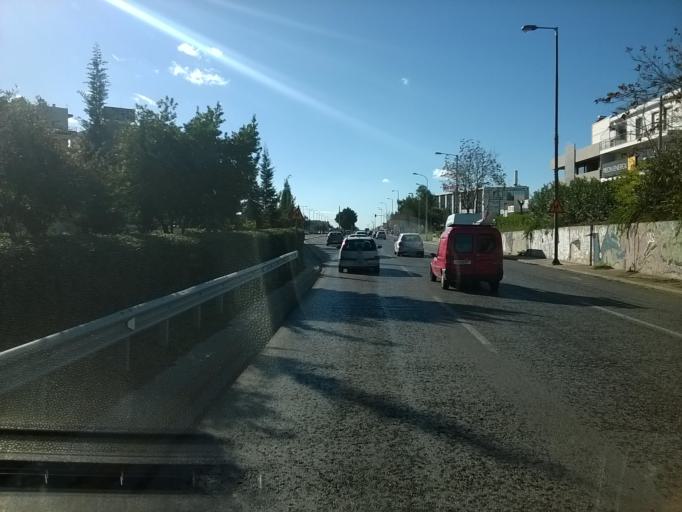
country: GR
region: Attica
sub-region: Nomarchia Athinas
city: Agios Dimitrios
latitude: 37.9257
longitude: 23.7443
